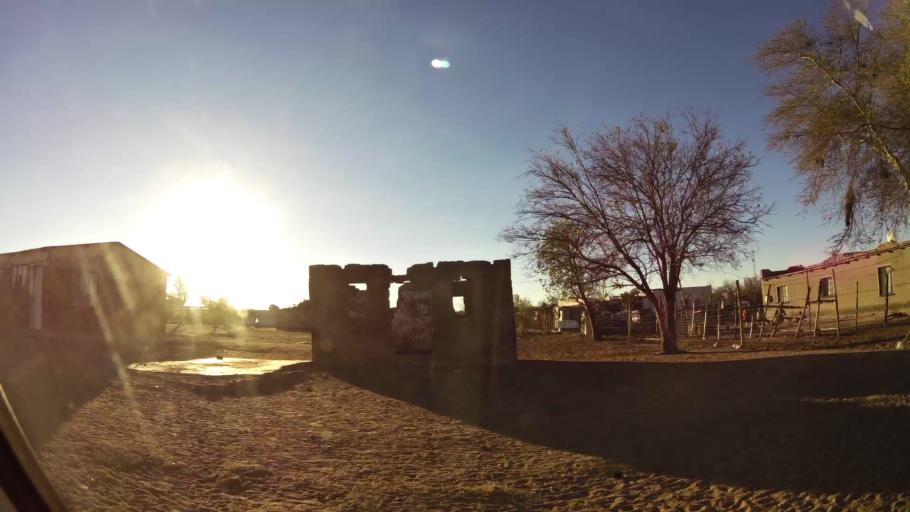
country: ZA
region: Limpopo
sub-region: Capricorn District Municipality
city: Polokwane
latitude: -23.8184
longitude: 29.3797
